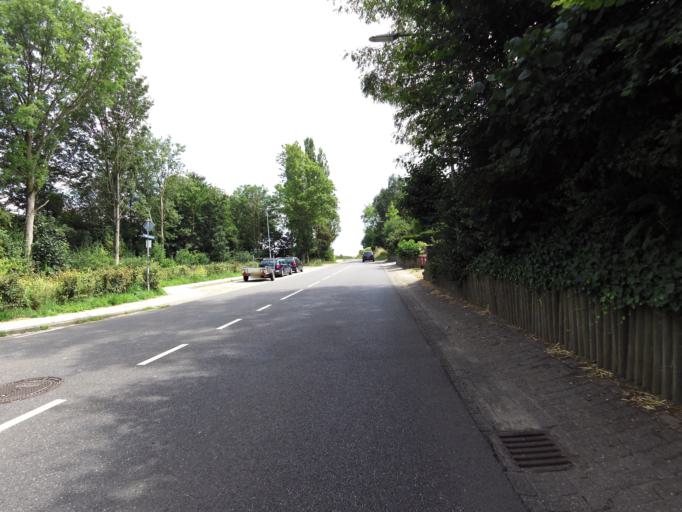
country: NL
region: Limburg
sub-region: Gemeente Voerendaal
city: Ubachsberg
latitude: 50.8076
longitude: 5.9217
